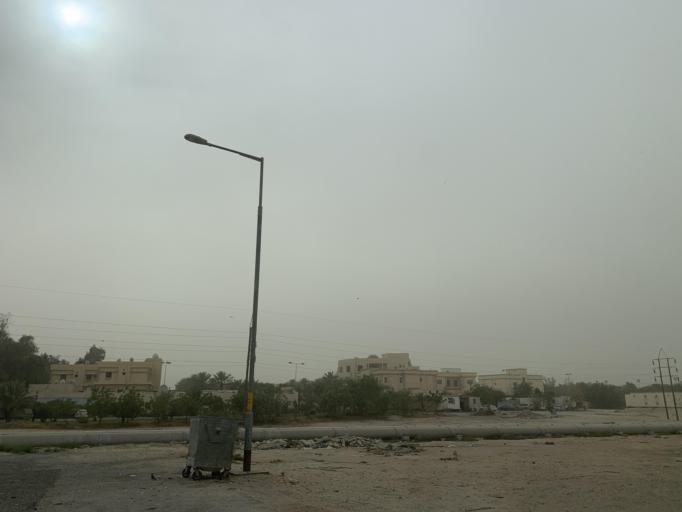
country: BH
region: Northern
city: Ar Rifa'
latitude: 26.1374
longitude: 50.5363
